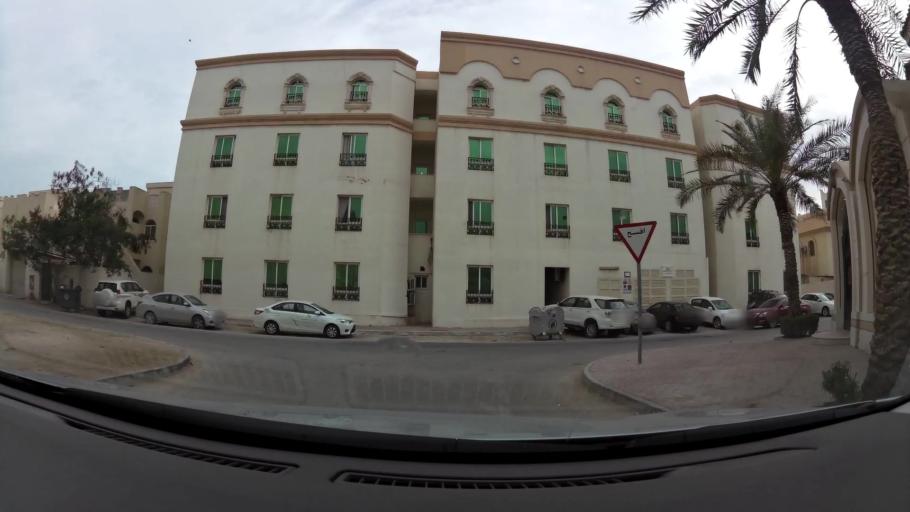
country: QA
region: Baladiyat ad Dawhah
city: Doha
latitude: 25.2757
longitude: 51.4958
